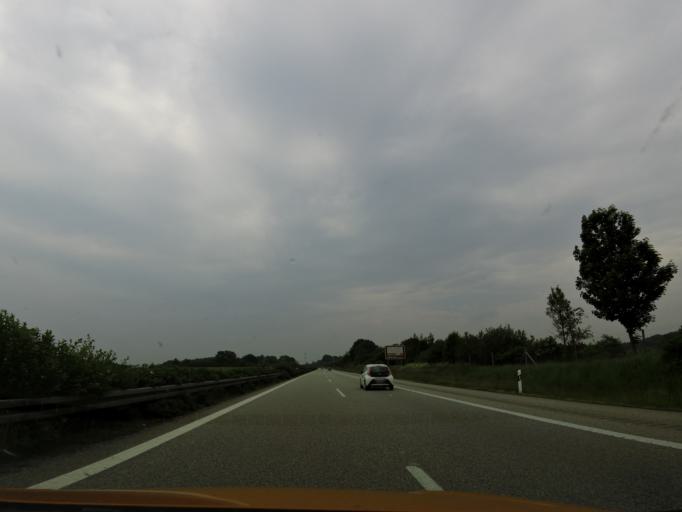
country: DE
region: Mecklenburg-Vorpommern
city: Grevesmuhlen
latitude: 53.8261
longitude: 11.1759
